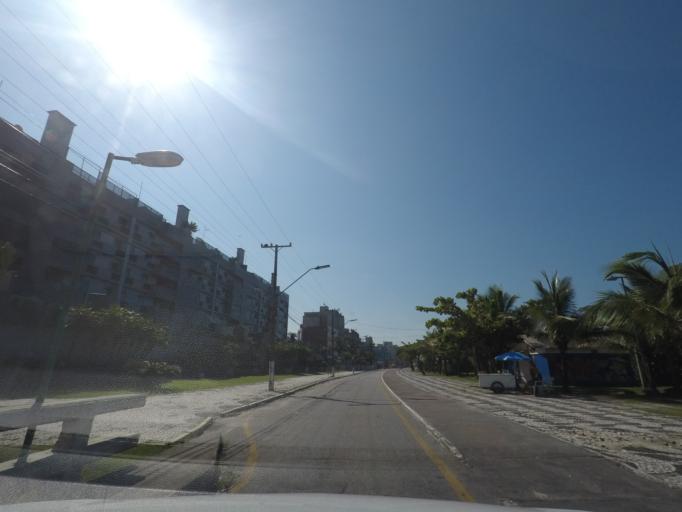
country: BR
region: Parana
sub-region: Guaratuba
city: Guaratuba
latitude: -25.8327
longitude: -48.5369
